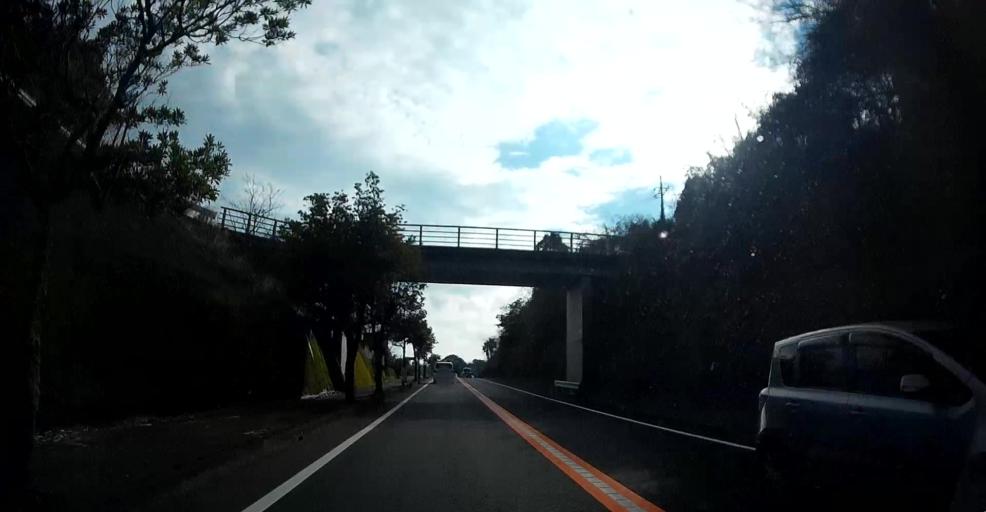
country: JP
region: Kumamoto
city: Yatsushiro
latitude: 32.5989
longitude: 130.4357
